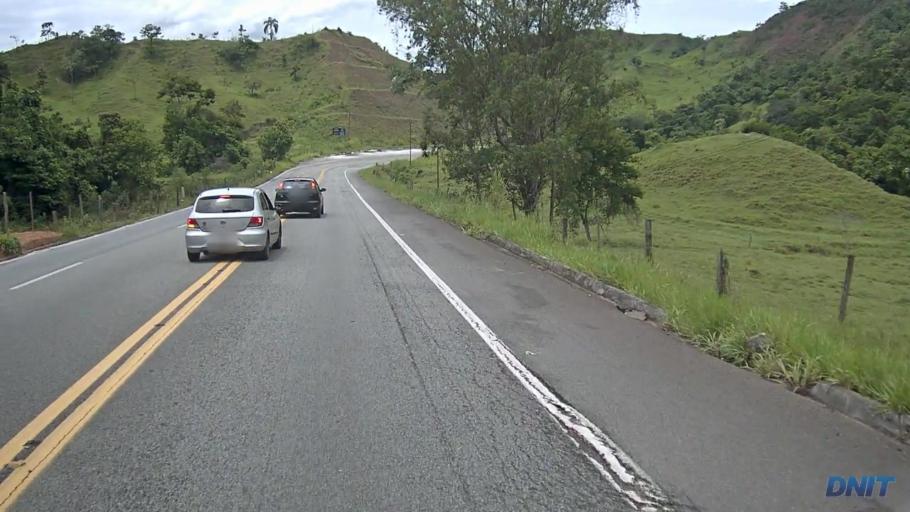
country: BR
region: Minas Gerais
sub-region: Nova Era
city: Nova Era
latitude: -19.6254
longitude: -42.8647
